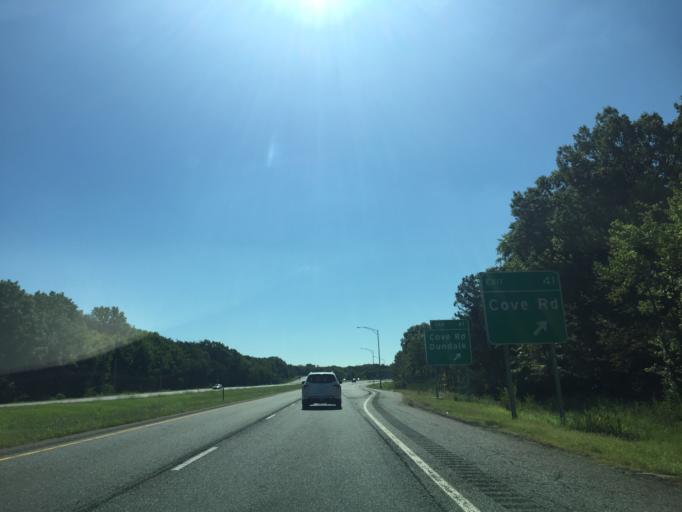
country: US
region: Maryland
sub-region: Baltimore County
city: Essex
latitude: 39.2806
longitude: -76.4798
